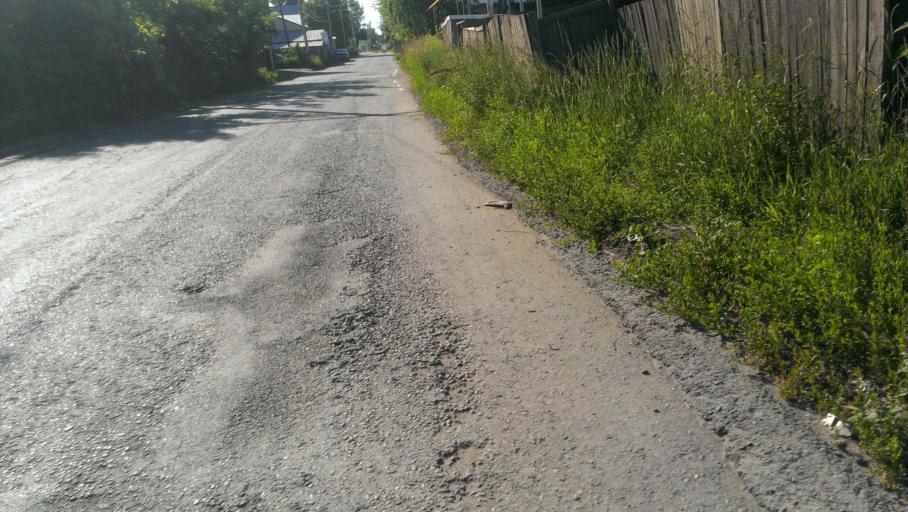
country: RU
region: Altai Krai
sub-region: Gorod Barnaulskiy
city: Barnaul
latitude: 53.3575
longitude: 83.7440
